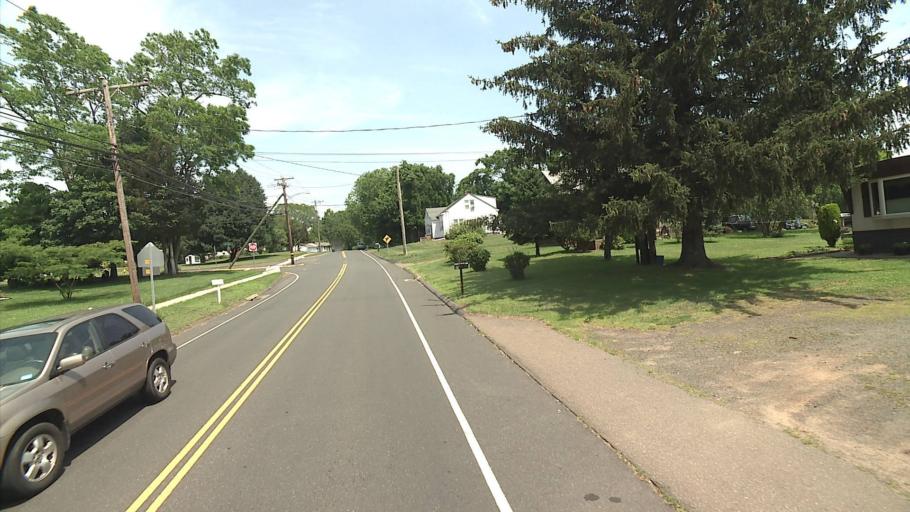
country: US
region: Connecticut
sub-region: New Haven County
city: Branford
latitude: 41.2950
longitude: -72.8199
